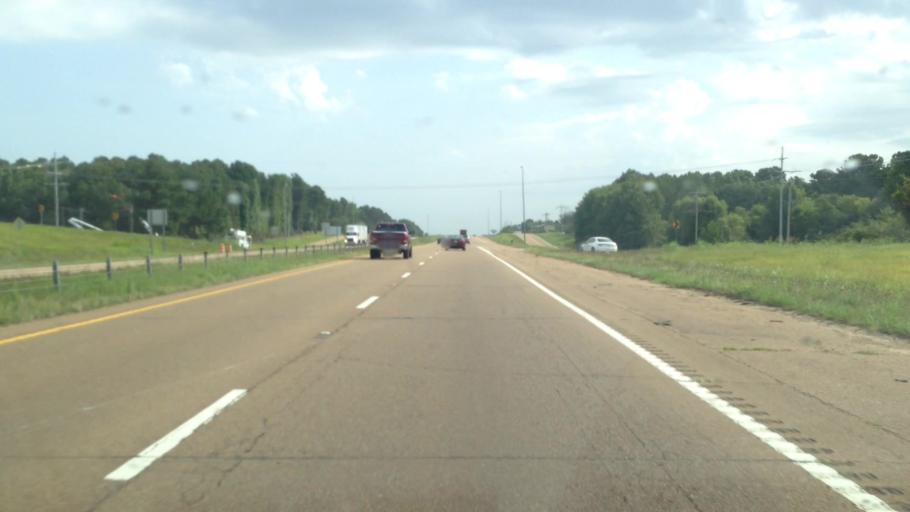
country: US
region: Mississippi
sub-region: Hinds County
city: Terry
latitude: 32.1328
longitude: -90.2865
